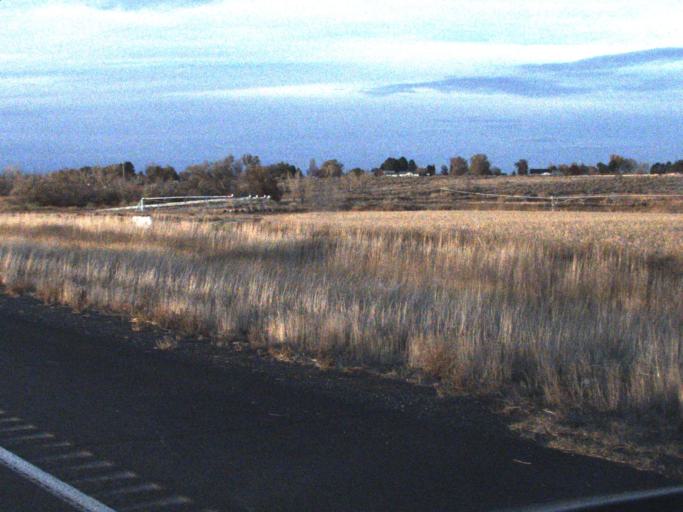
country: US
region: Washington
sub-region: Walla Walla County
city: Burbank
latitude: 46.2019
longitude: -119.0022
